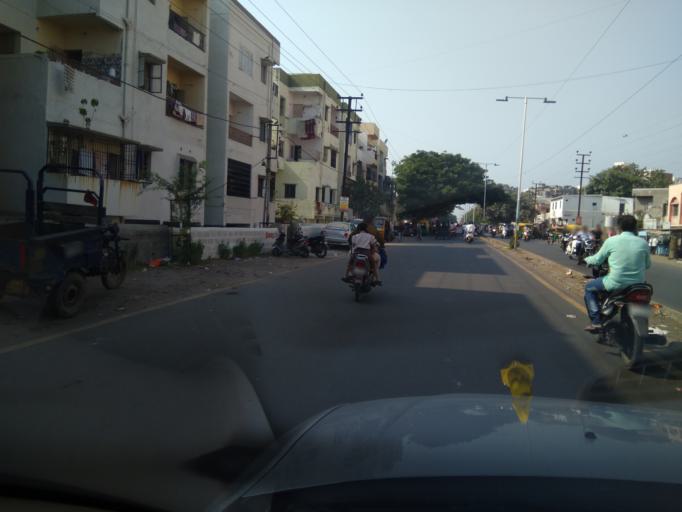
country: IN
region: Gujarat
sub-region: Jamnagar
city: Jamnagar
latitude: 22.4653
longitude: 70.0526
